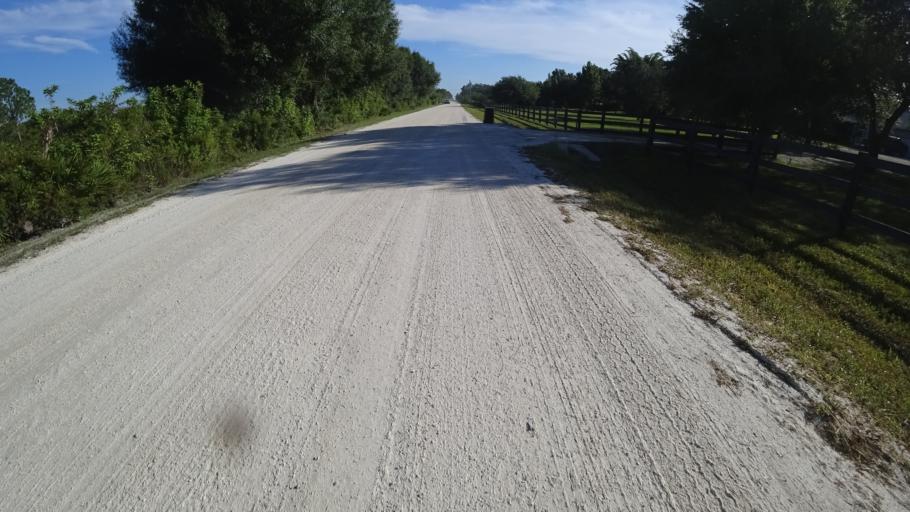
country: US
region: Florida
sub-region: Sarasota County
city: Fruitville
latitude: 27.4158
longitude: -82.2614
